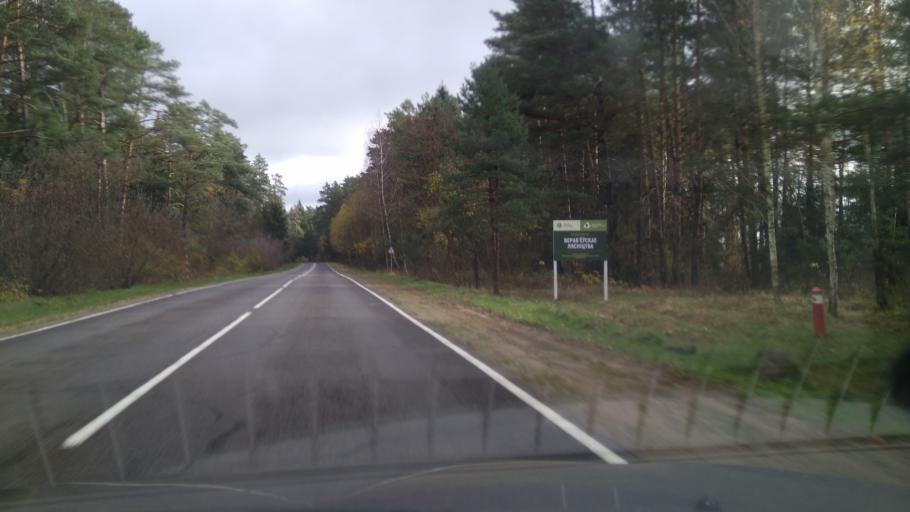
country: BY
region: Minsk
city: Slutsk
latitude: 53.2191
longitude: 27.5726
